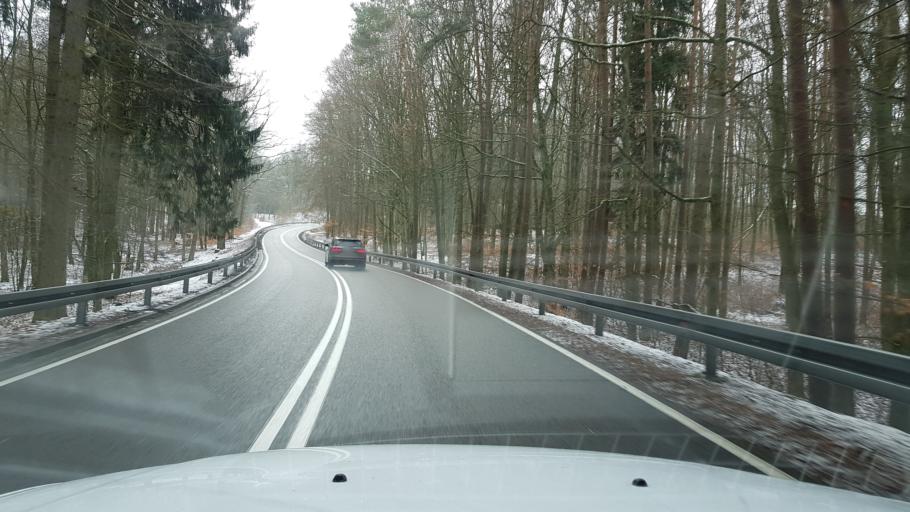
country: PL
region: West Pomeranian Voivodeship
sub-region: Powiat drawski
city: Wierzchowo
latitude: 53.5404
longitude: 16.0991
